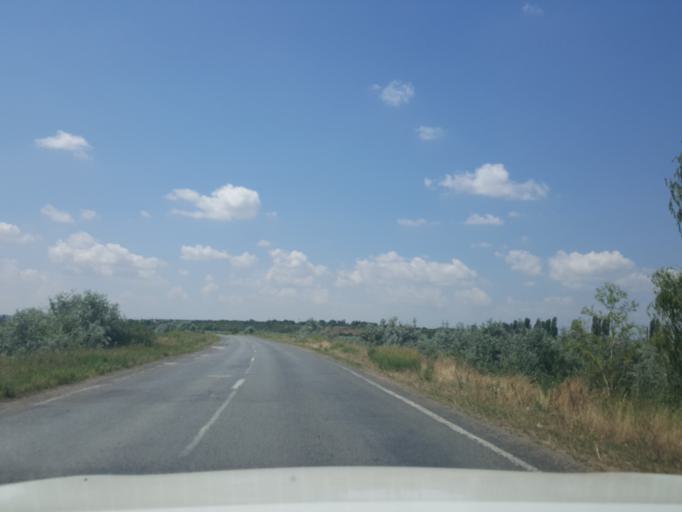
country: UA
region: Odessa
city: Bilyayivka
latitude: 46.4124
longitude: 30.1164
